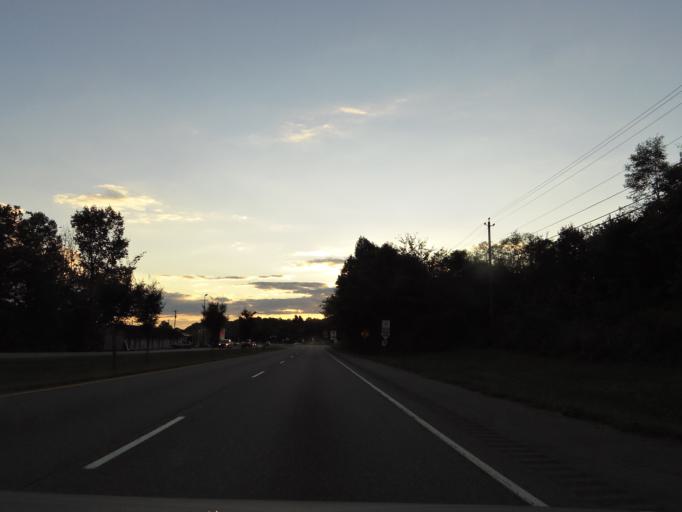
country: US
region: Tennessee
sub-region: Knox County
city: Mascot
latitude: 36.0172
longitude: -83.8226
